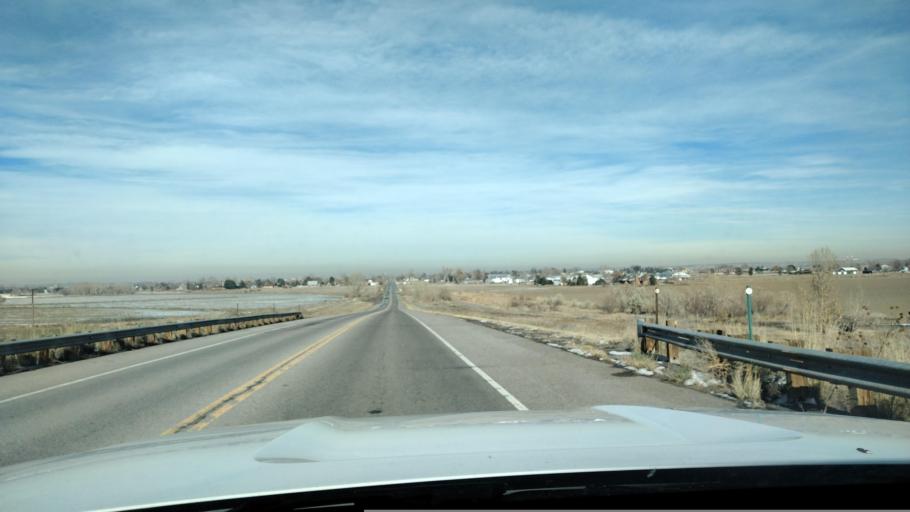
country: US
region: Colorado
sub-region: Adams County
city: Brighton
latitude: 39.9287
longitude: -104.8184
